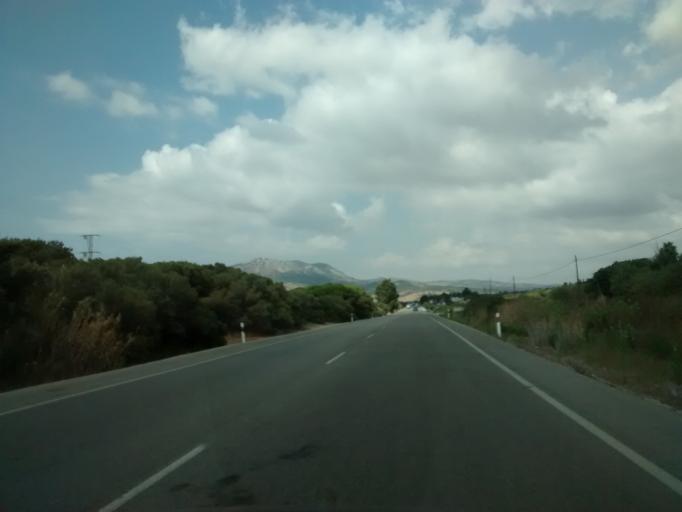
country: ES
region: Andalusia
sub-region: Provincia de Cadiz
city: Tarifa
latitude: 36.0617
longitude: -5.6711
